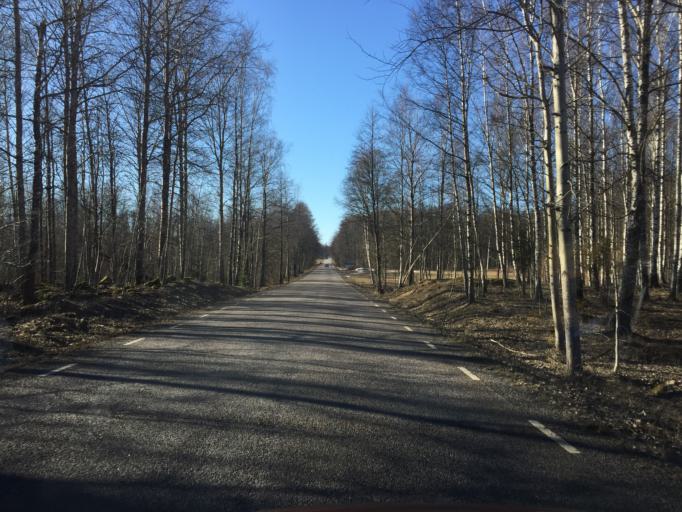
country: SE
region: OErebro
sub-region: Orebro Kommun
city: Odensbacken
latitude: 59.0143
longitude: 15.6008
